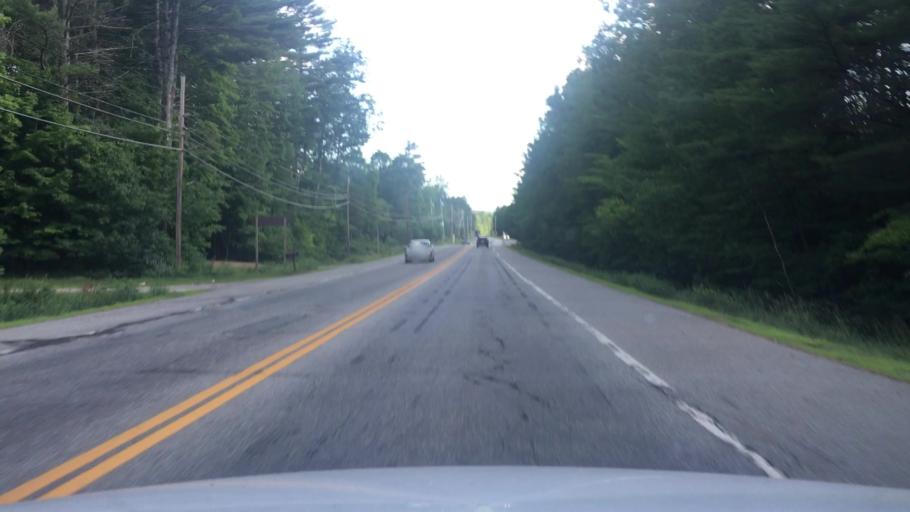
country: US
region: Maine
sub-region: Franklin County
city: Wilton
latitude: 44.5708
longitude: -70.2301
